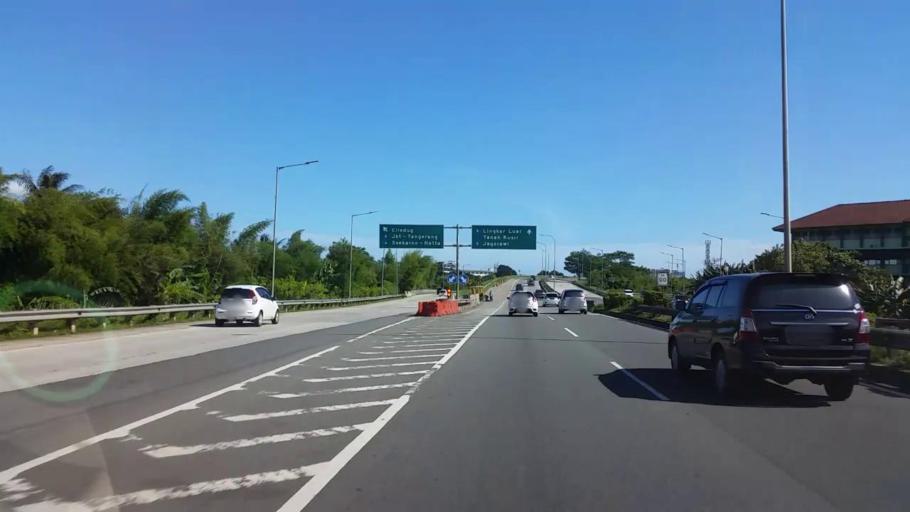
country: ID
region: Banten
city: South Tangerang
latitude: -6.2536
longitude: 106.7612
